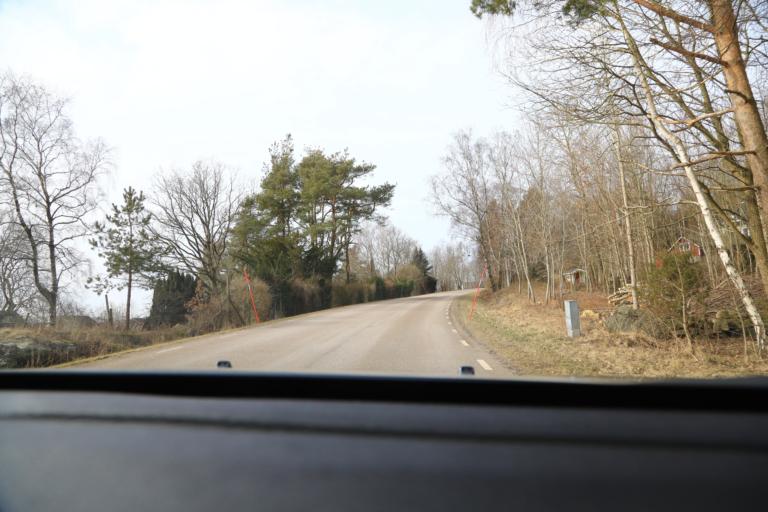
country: SE
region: Halland
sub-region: Kungsbacka Kommun
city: Frillesas
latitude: 57.2319
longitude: 12.2157
